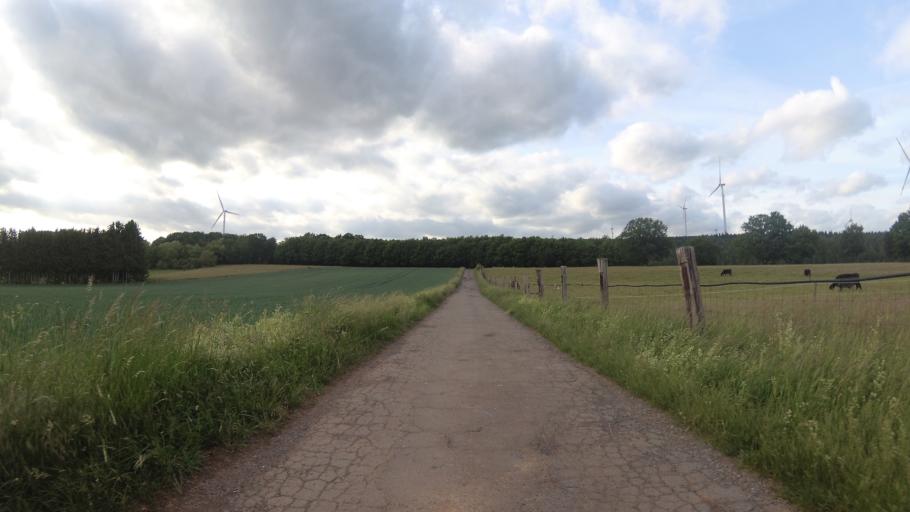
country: DE
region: Saarland
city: Hangard
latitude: 49.4236
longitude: 7.2069
